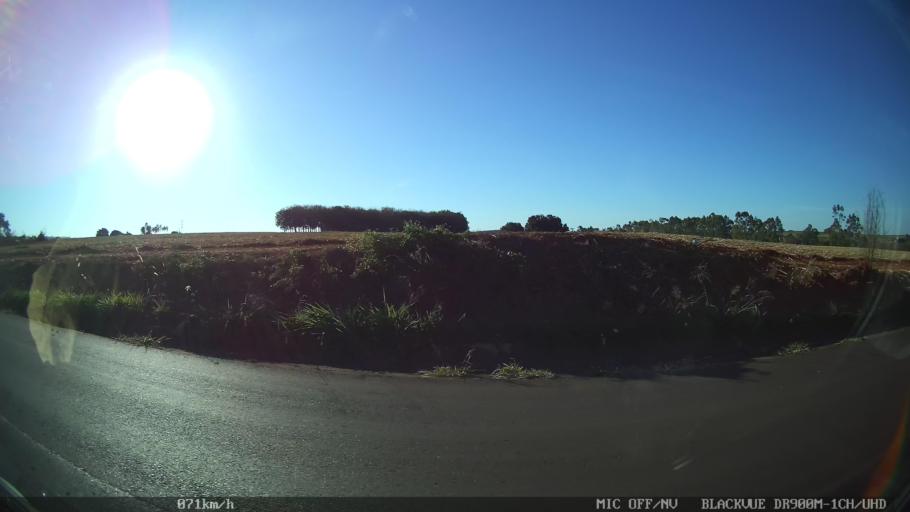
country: BR
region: Sao Paulo
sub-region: Guapiacu
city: Guapiacu
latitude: -20.7707
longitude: -49.2169
